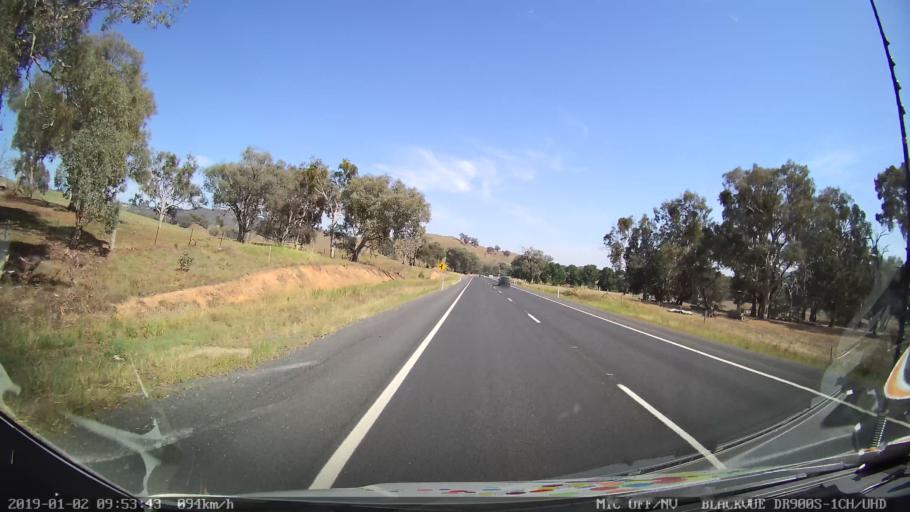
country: AU
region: New South Wales
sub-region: Tumut Shire
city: Tumut
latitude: -35.2445
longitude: 148.2006
